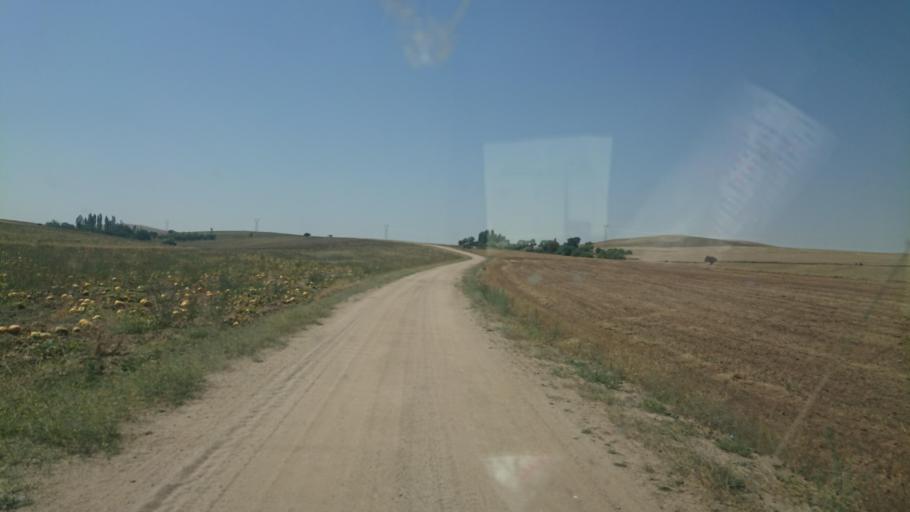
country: TR
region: Aksaray
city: Agacoren
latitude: 38.8099
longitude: 33.9517
